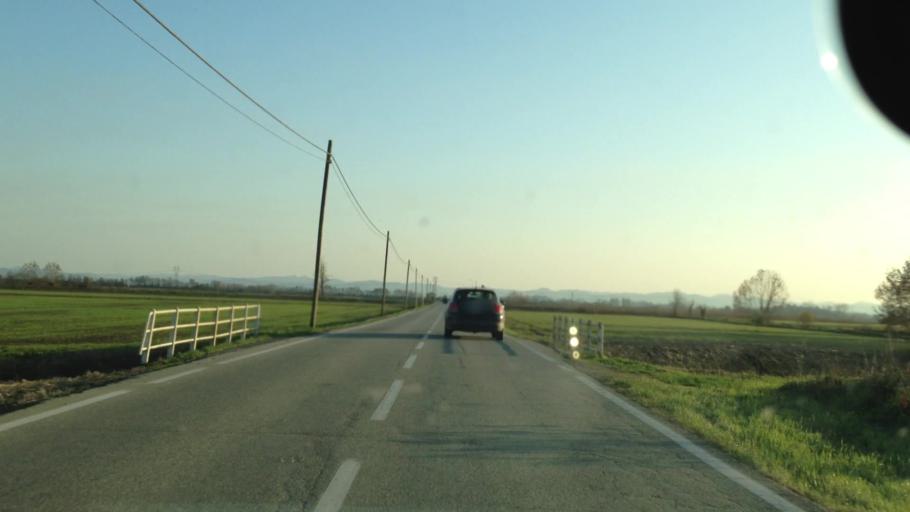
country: IT
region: Piedmont
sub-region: Provincia di Vercelli
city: Livorno Ferraris
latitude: 45.2564
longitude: 8.0860
